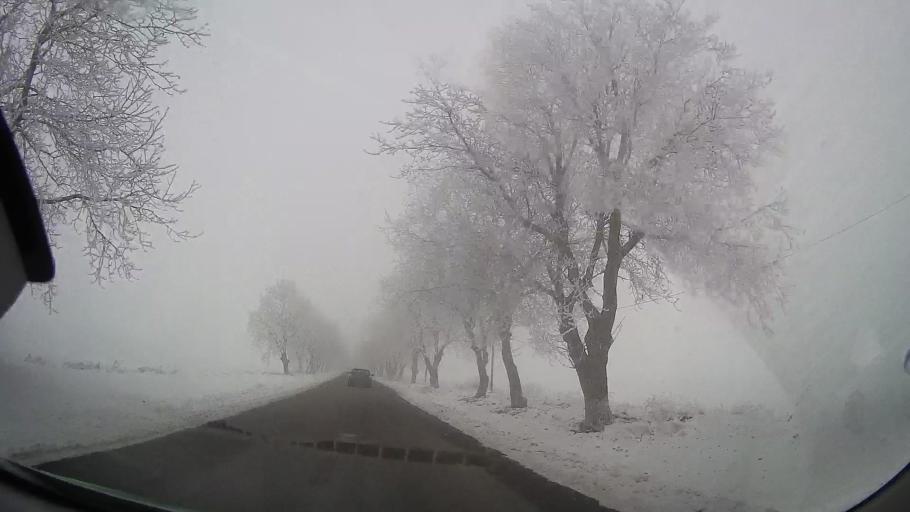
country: RO
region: Neamt
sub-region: Comuna Cordun
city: Cordun
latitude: 46.9825
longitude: 26.8651
